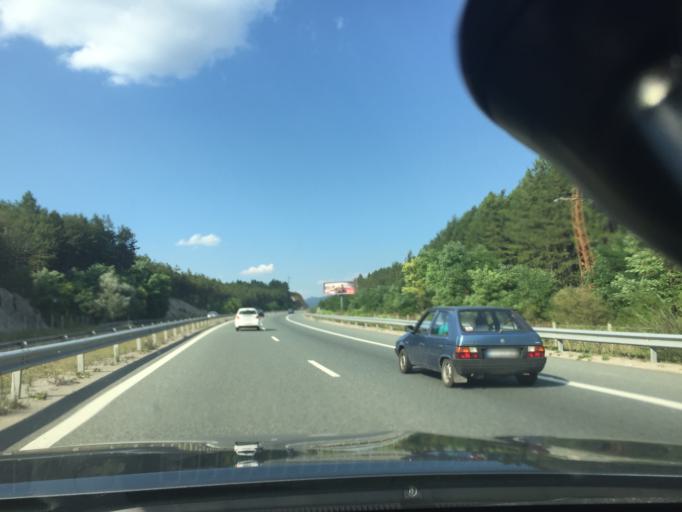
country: BG
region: Pernik
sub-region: Obshtina Pernik
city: Pernik
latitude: 42.4938
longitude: 23.1341
